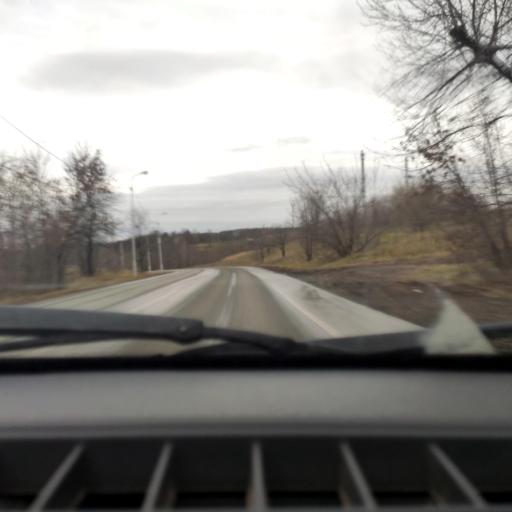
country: RU
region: Bashkortostan
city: Ufa
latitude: 54.8659
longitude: 56.0721
